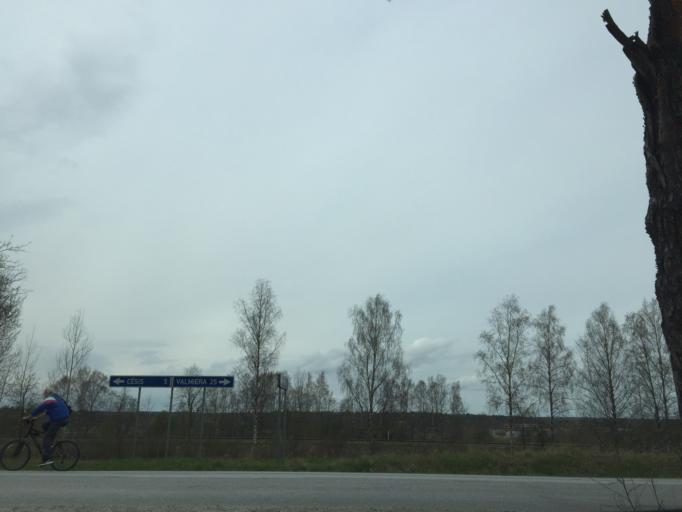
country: LV
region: Priekuli
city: Priekuli
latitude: 57.3455
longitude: 25.3432
